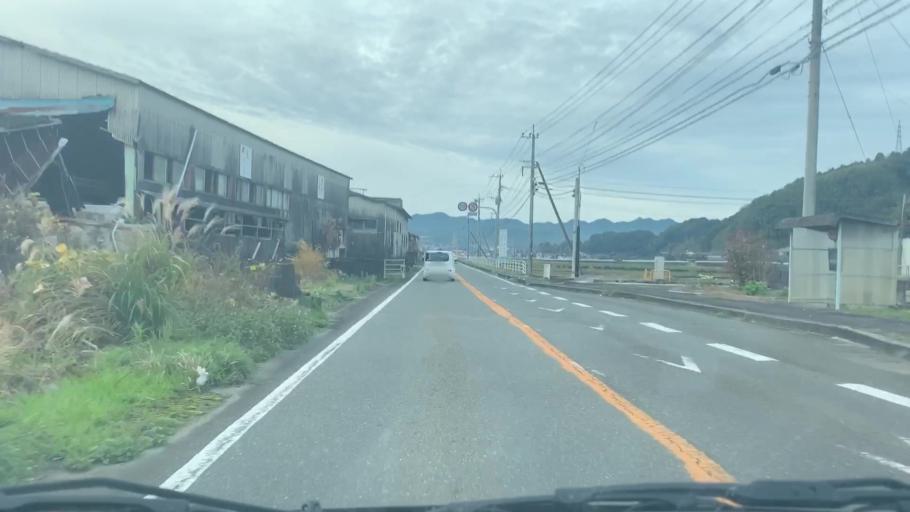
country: JP
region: Saga Prefecture
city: Ureshinomachi-shimojuku
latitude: 33.1352
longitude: 130.0151
